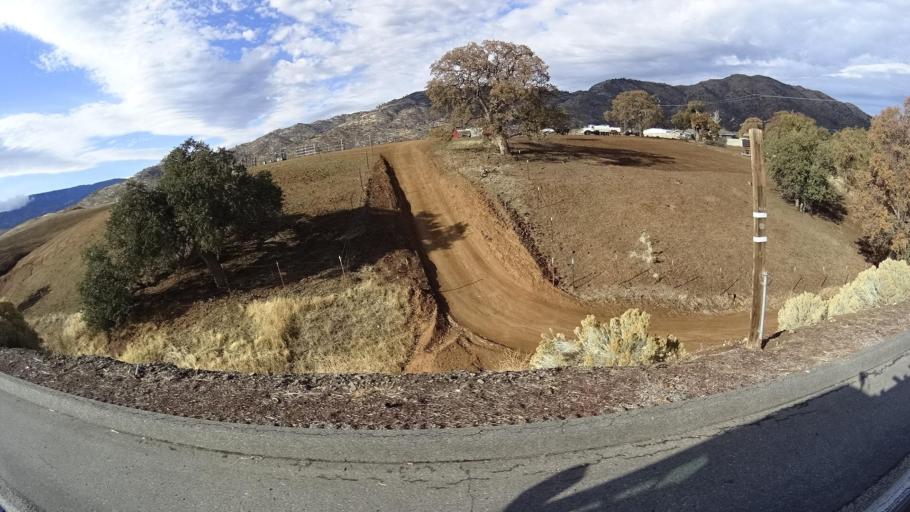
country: US
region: California
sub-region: Kern County
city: Golden Hills
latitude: 35.1387
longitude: -118.4948
